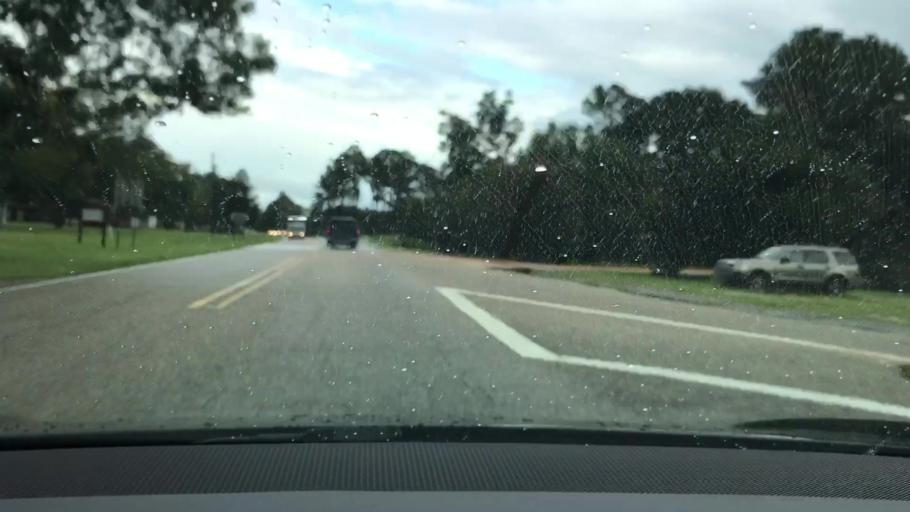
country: US
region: Alabama
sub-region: Geneva County
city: Samson
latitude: 31.1165
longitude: -86.1201
